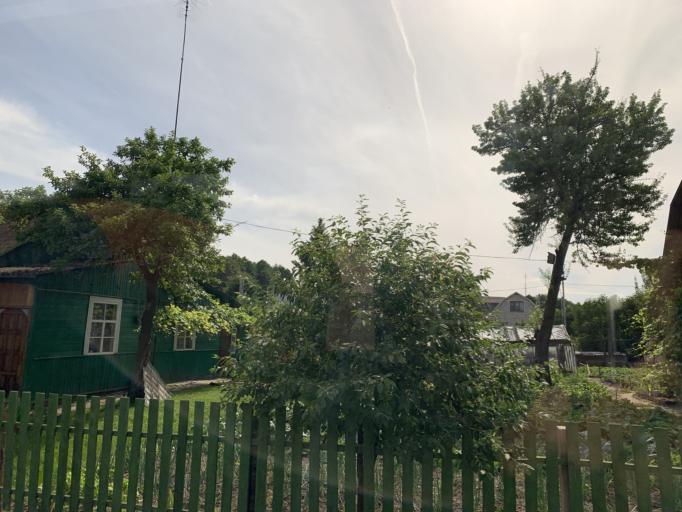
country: BY
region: Minsk
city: Novy Svyerzhan'
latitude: 53.4506
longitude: 26.7372
